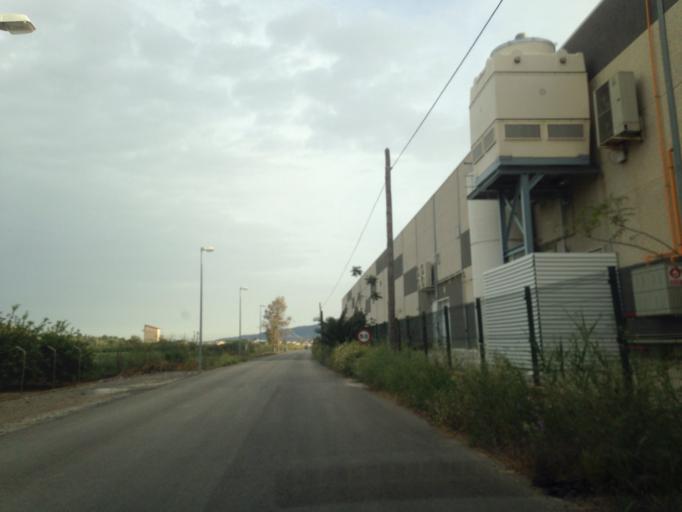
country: ES
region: Andalusia
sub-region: Provincia de Malaga
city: Alhaurin de la Torre
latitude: 36.7339
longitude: -4.5428
